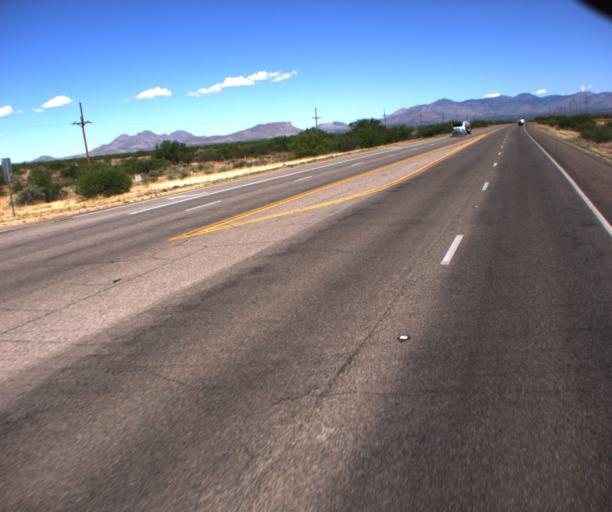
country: US
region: Arizona
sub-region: Cochise County
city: Huachuca City
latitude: 31.5943
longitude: -110.3245
